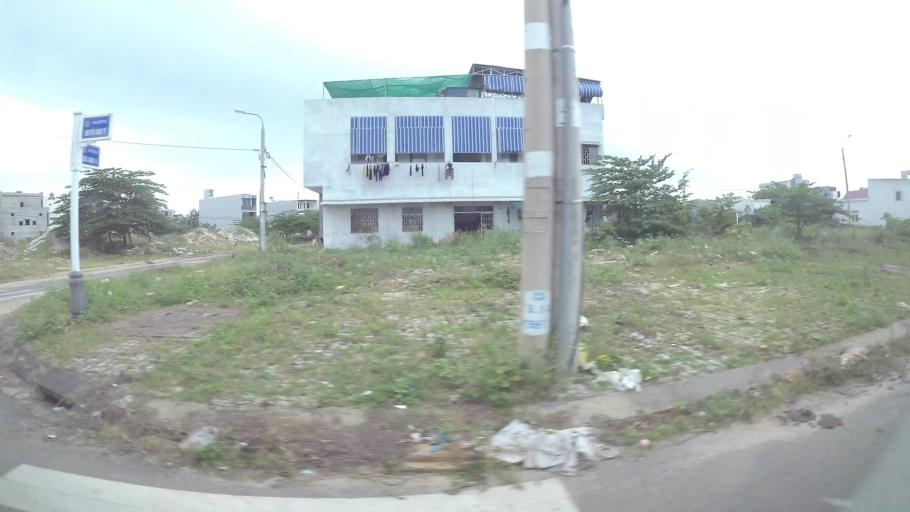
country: VN
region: Da Nang
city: Lien Chieu
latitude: 16.0506
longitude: 108.1668
